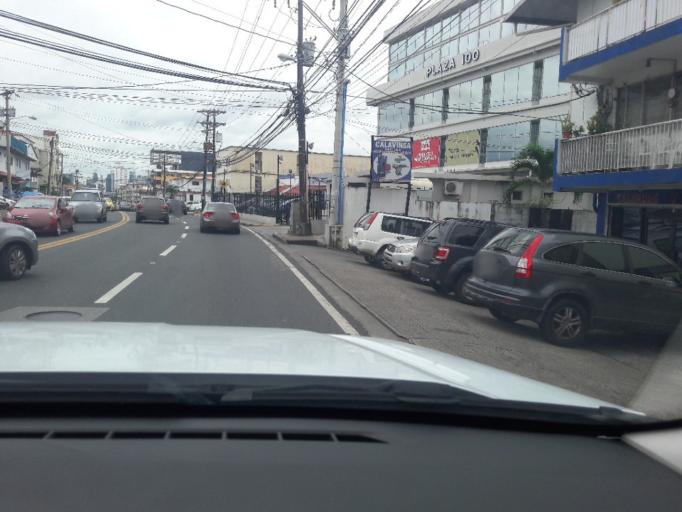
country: PA
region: Panama
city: Panama
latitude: 9.0143
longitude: -79.5222
